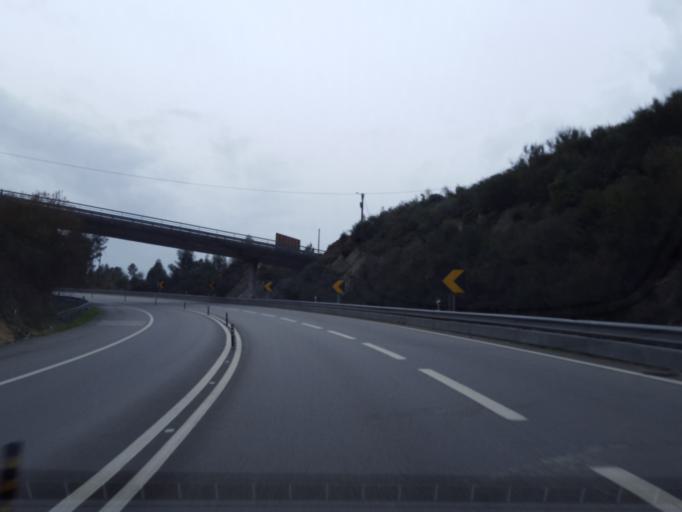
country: PT
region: Porto
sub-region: Marco de Canaveses
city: Marco de Canavezes
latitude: 41.2145
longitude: -8.1689
